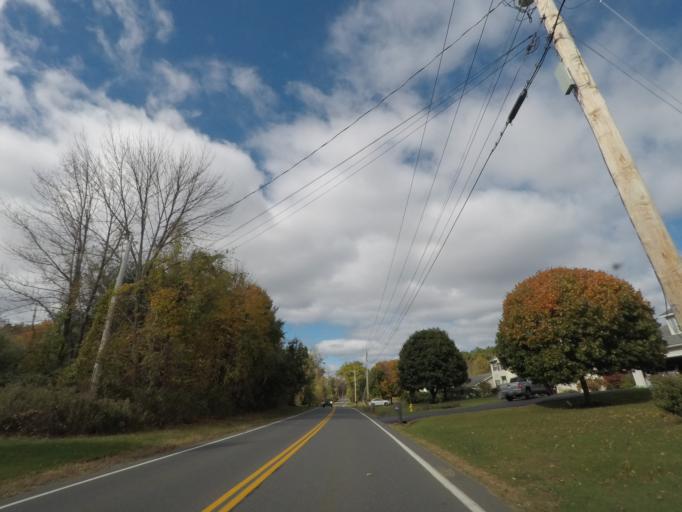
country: US
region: New York
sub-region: Albany County
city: Cohoes
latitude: 42.8294
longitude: -73.7497
